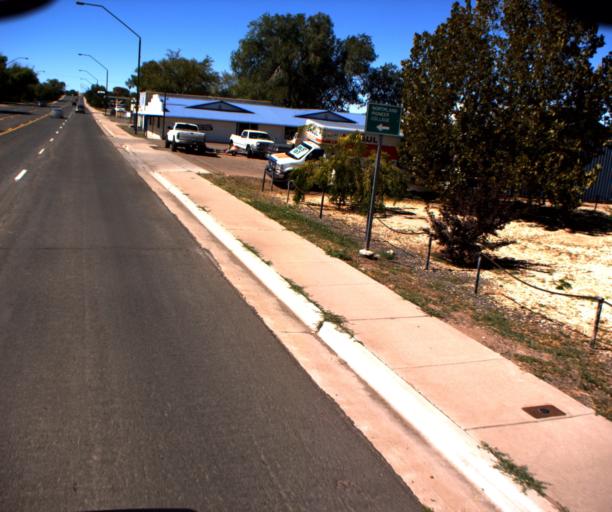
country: US
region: Arizona
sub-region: Apache County
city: Saint Johns
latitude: 34.5068
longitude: -109.3693
